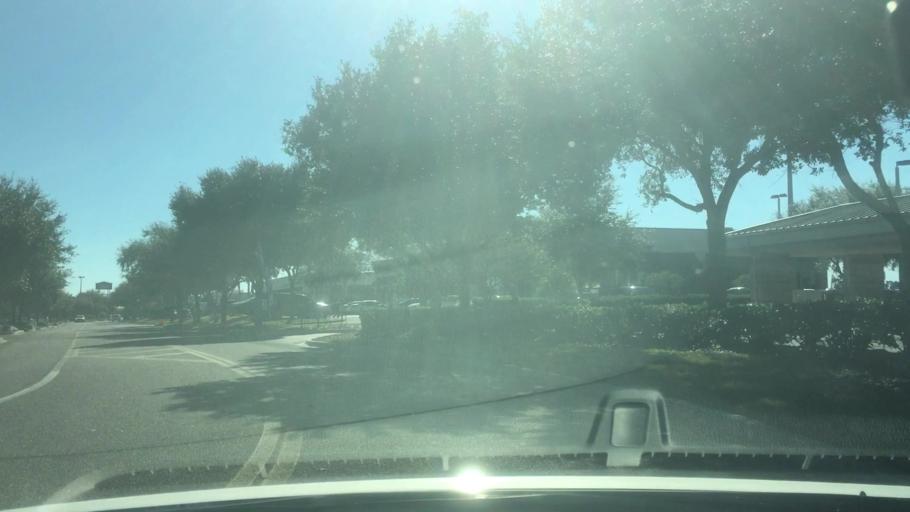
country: US
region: Florida
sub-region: Duval County
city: Jacksonville
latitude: 30.3365
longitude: -81.5510
